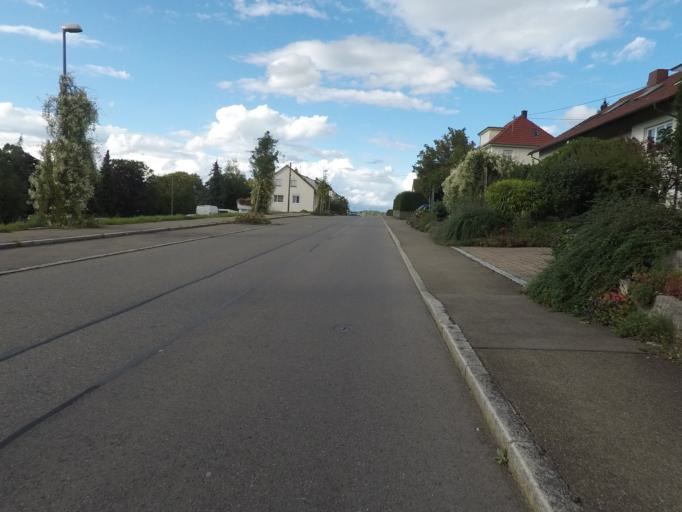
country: DE
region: Baden-Wuerttemberg
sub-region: Tuebingen Region
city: Pfullingen
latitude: 48.4666
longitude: 9.2317
